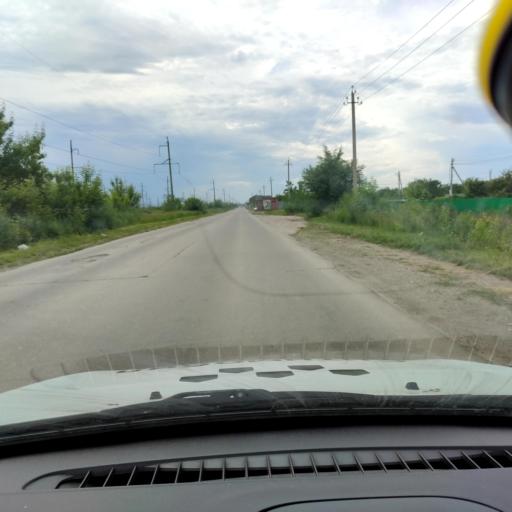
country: RU
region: Samara
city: Tol'yatti
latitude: 53.5896
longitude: 49.3192
